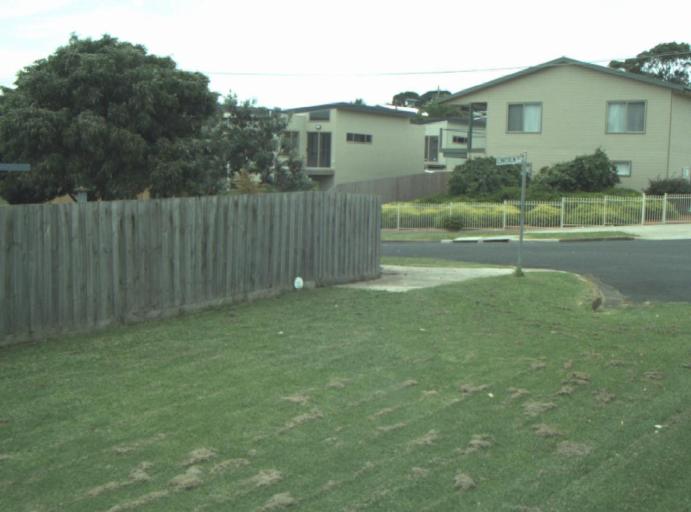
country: AU
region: Victoria
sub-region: Greater Geelong
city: Clifton Springs
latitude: -38.1197
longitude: 144.6438
